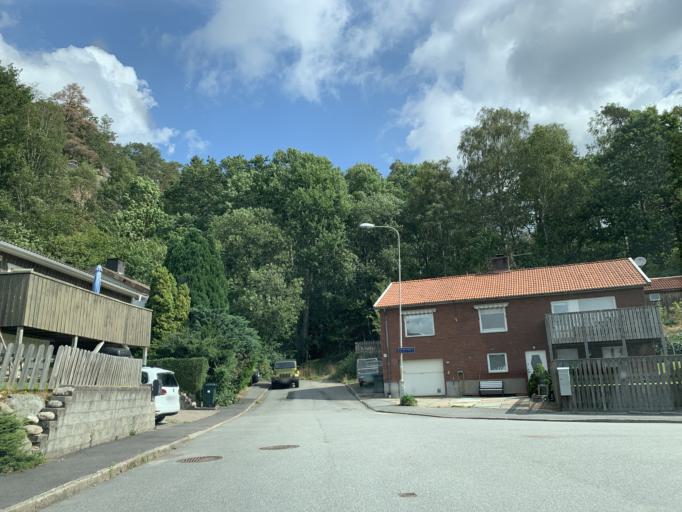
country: SE
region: Vaestra Goetaland
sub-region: Goteborg
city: Eriksbo
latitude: 57.7477
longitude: 12.0515
